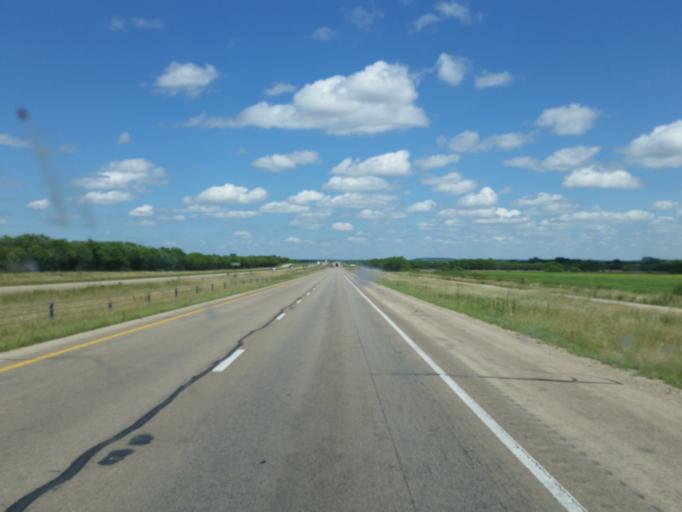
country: US
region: Texas
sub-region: Callahan County
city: Baird
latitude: 32.3879
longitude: -99.3161
